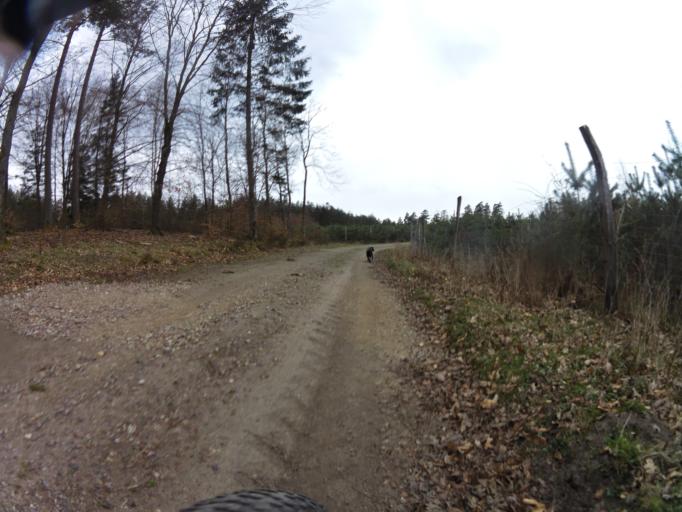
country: PL
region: West Pomeranian Voivodeship
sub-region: Powiat koszalinski
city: Polanow
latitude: 54.0690
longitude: 16.6233
